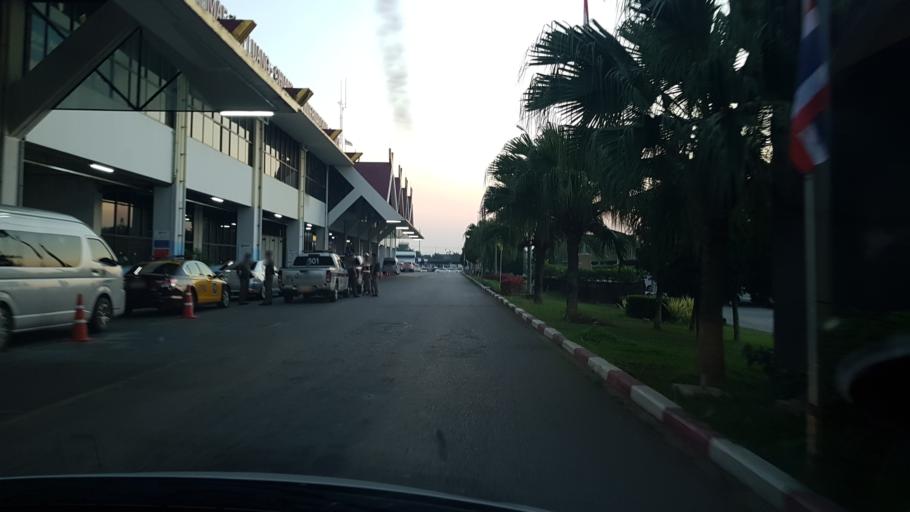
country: TH
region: Chiang Rai
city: Chiang Rai
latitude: 19.9549
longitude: 99.8790
